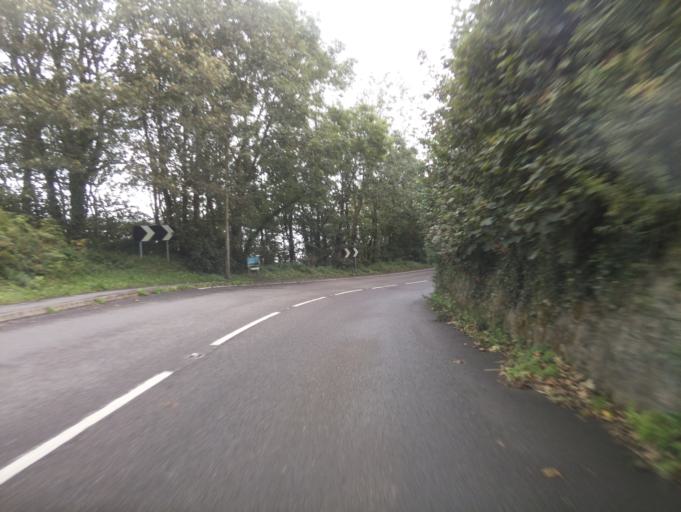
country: GB
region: England
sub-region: Devon
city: Dartmouth
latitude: 50.2714
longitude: -3.6576
